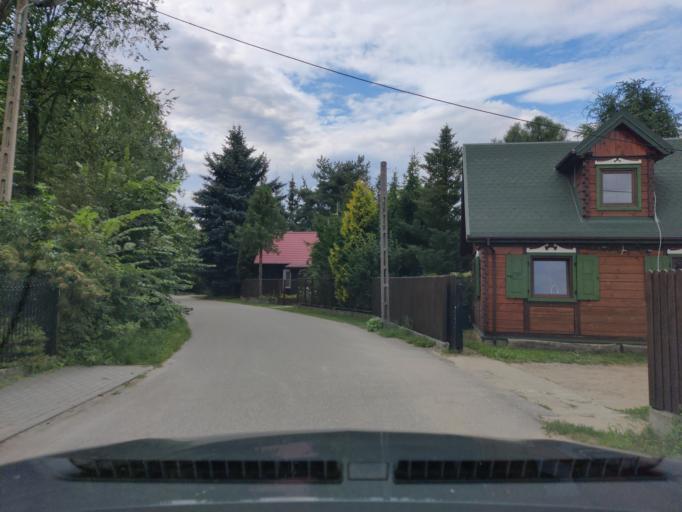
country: PL
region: Masovian Voivodeship
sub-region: Powiat pultuski
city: Pultusk
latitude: 52.7265
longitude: 21.1206
